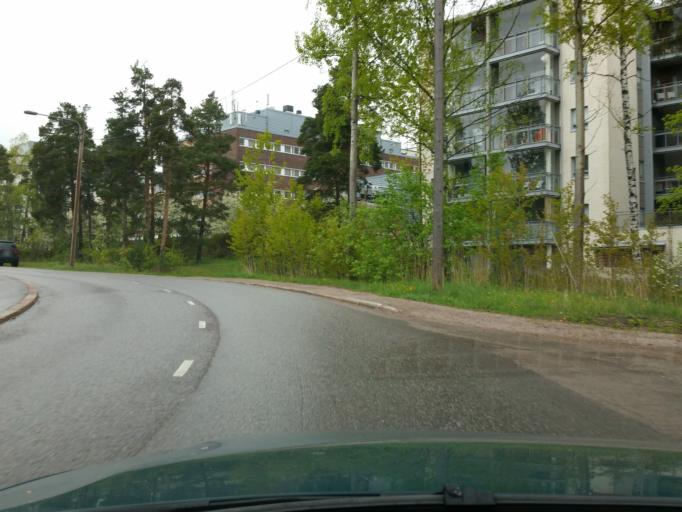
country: FI
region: Uusimaa
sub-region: Helsinki
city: Teekkarikylae
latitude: 60.2209
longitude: 24.8340
